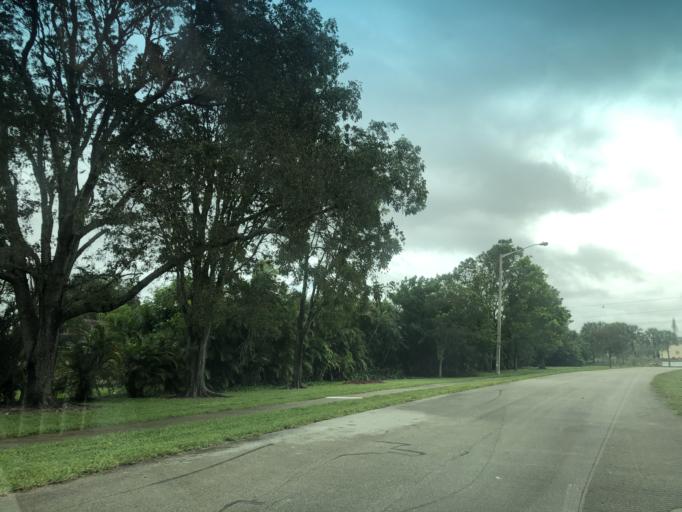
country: US
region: Florida
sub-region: Broward County
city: North Lauderdale
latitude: 26.2316
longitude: -80.2370
